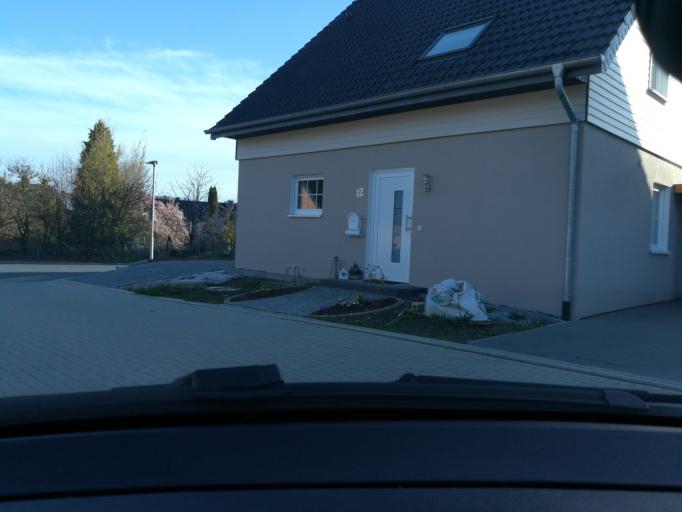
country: DE
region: North Rhine-Westphalia
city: Borgholzhausen
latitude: 52.1062
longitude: 8.3038
